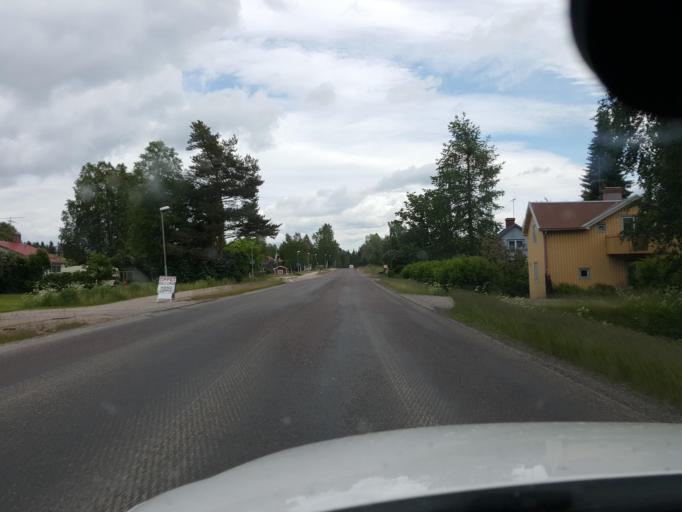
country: SE
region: Gaevleborg
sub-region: Ljusdals Kommun
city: Farila
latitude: 61.8013
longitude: 15.8787
